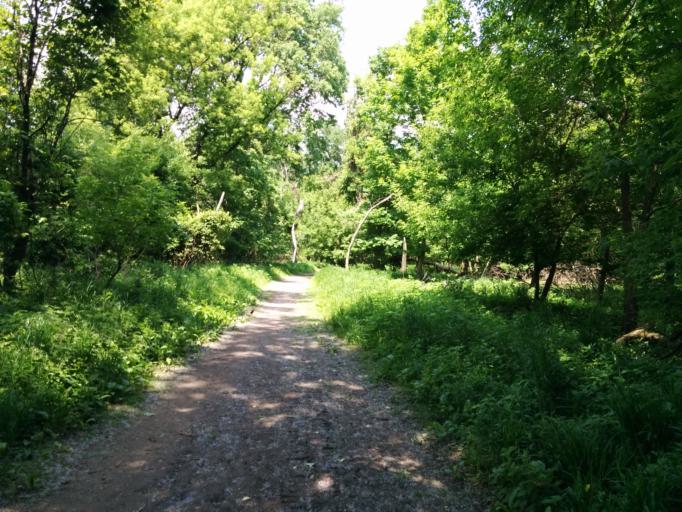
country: US
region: Illinois
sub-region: Cook County
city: River Grove
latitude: 41.9249
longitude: -87.8417
